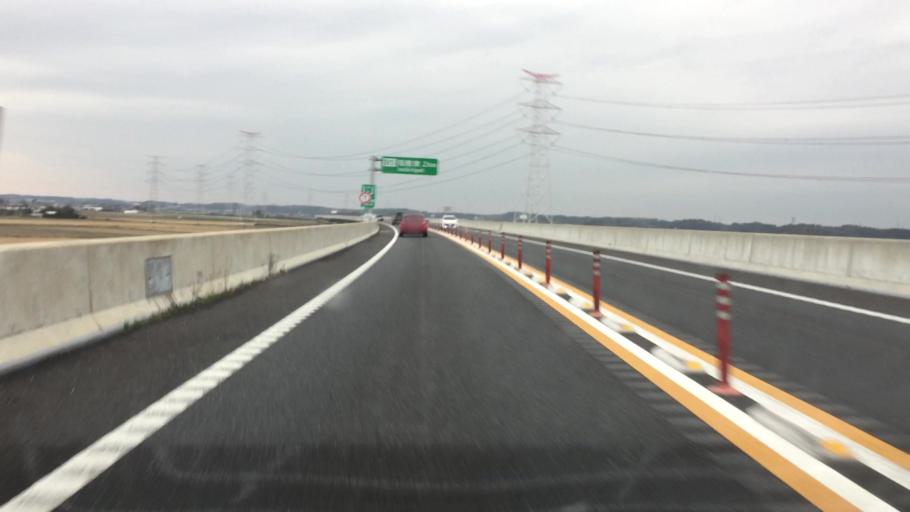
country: JP
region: Ibaraki
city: Inashiki
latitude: 35.9118
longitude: 140.3670
